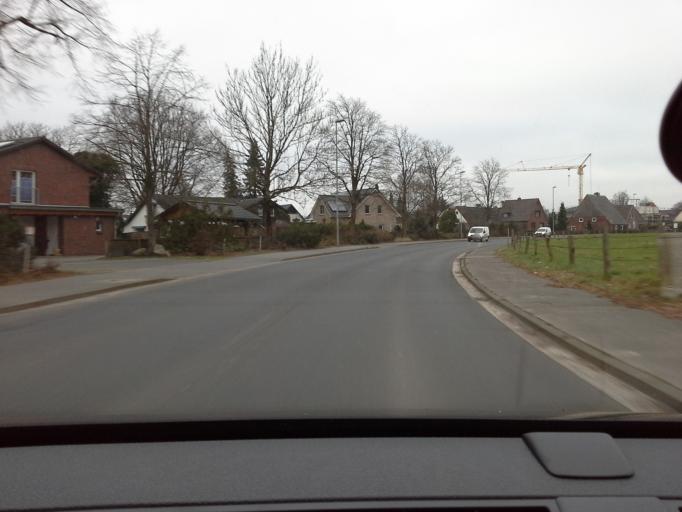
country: DE
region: Schleswig-Holstein
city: Quickborn
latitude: 53.7296
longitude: 9.8898
